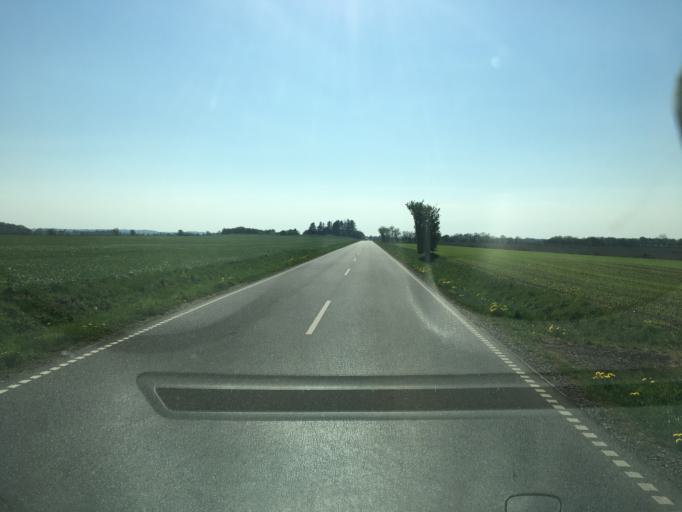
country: DK
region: South Denmark
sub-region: Haderslev Kommune
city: Vojens
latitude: 55.3083
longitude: 9.2757
